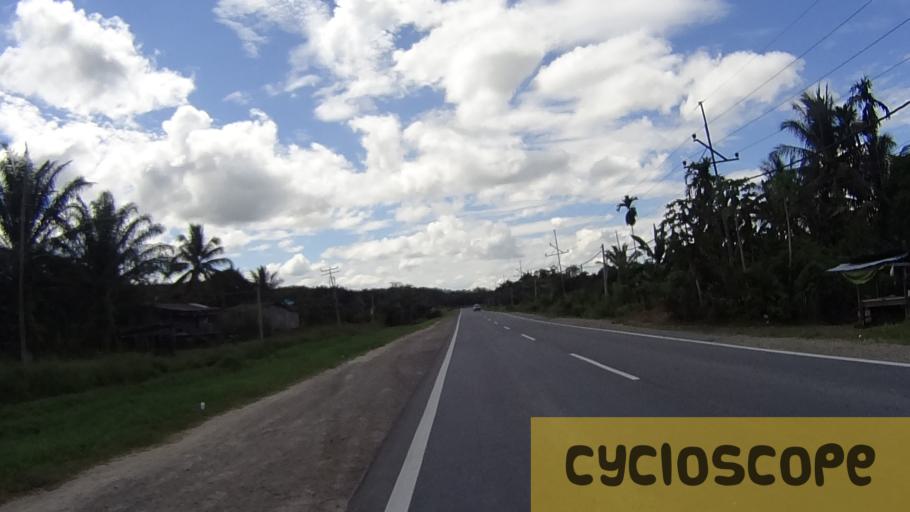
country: MY
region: Sabah
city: Beaufort
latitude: 5.3026
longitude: 115.6969
